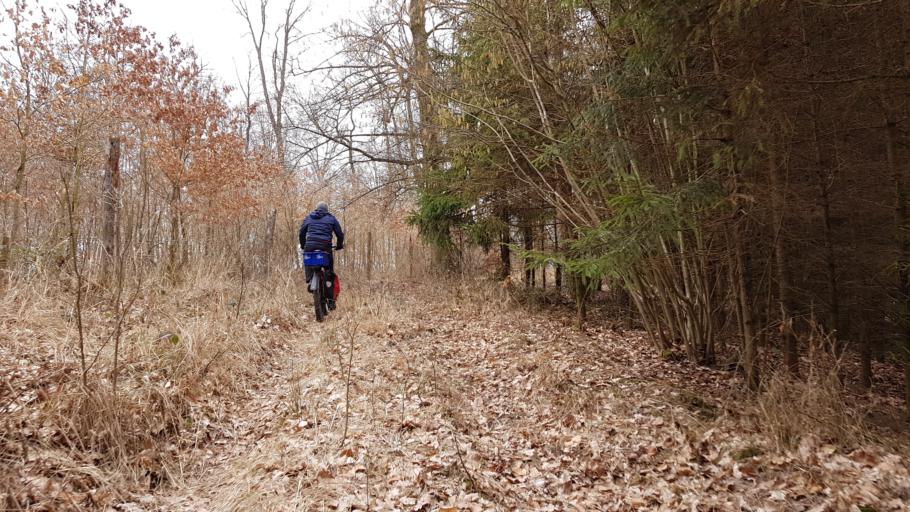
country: PL
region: West Pomeranian Voivodeship
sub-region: Powiat pyrzycki
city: Kozielice
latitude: 53.0720
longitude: 14.7516
